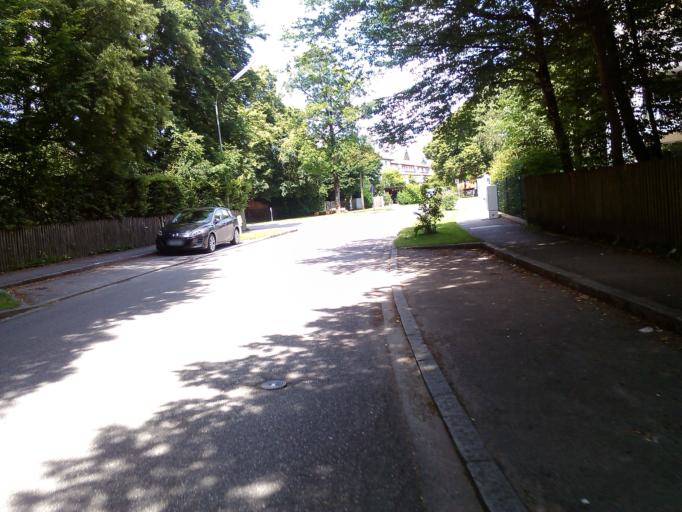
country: DE
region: Bavaria
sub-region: Upper Bavaria
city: Gauting
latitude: 48.0703
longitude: 11.3646
